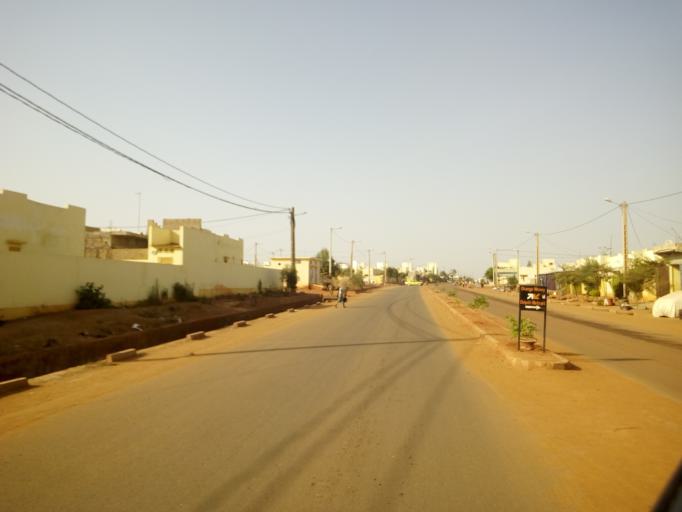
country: ML
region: Bamako
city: Bamako
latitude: 12.5790
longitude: -7.8594
